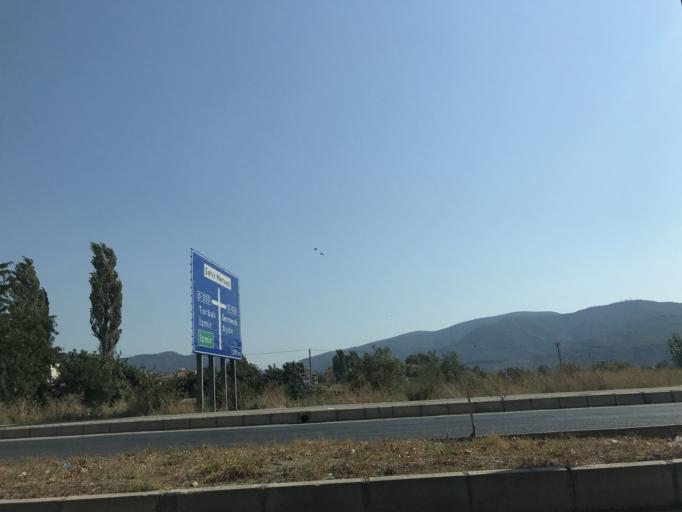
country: TR
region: Izmir
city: Selcuk
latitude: 37.9481
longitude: 27.3649
